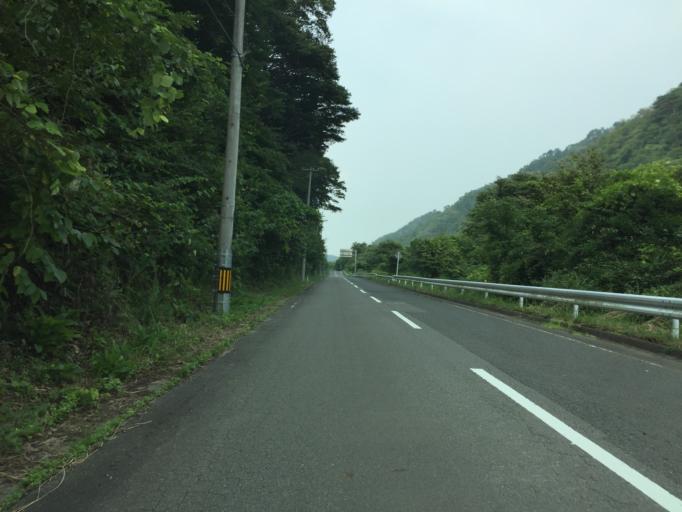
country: JP
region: Fukushima
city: Namie
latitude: 37.5787
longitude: 140.8838
